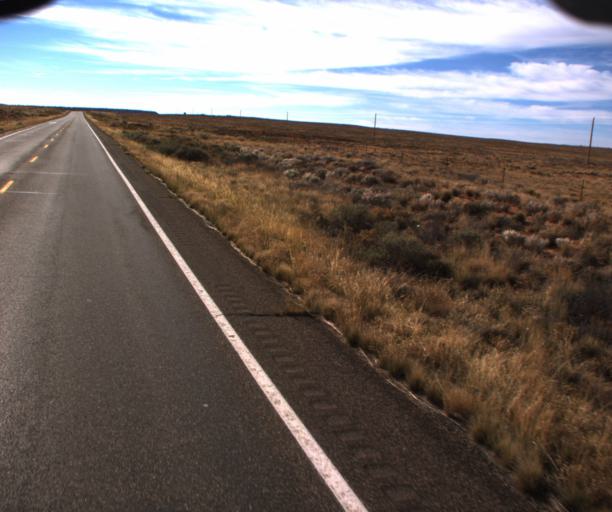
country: US
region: Arizona
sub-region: Coconino County
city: Kaibito
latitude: 36.7108
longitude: -111.2712
